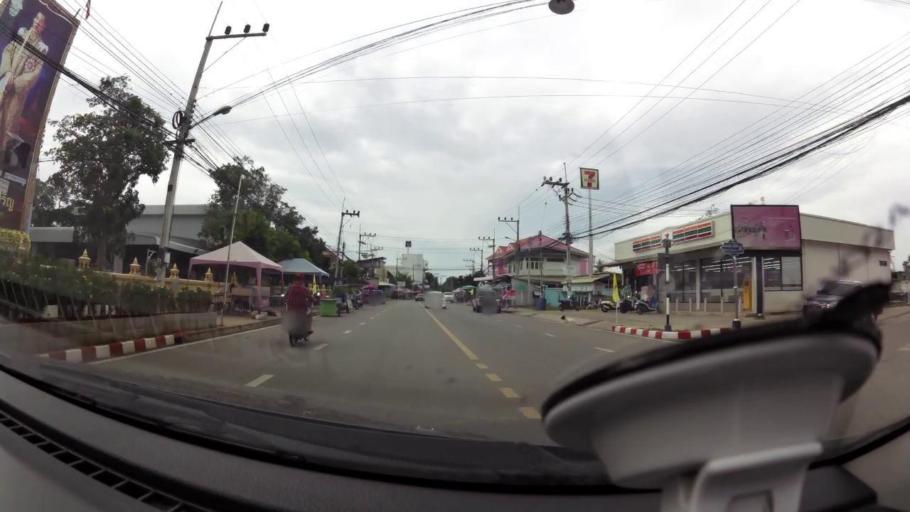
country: TH
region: Prachuap Khiri Khan
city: Pran Buri
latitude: 12.3972
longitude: 99.9899
